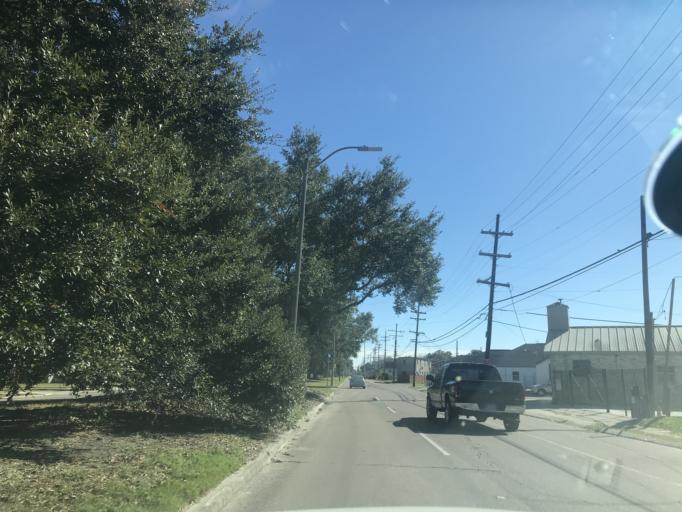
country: US
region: Louisiana
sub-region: Orleans Parish
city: New Orleans
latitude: 29.9508
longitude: -90.0965
